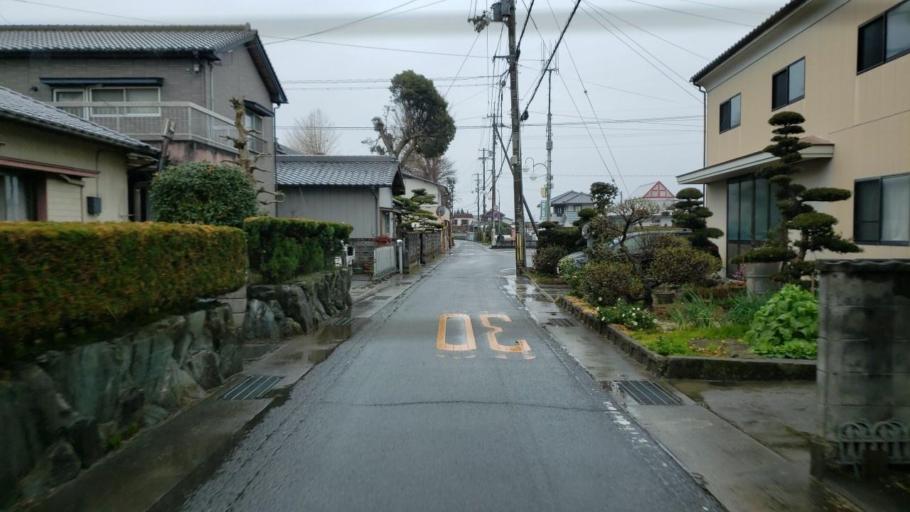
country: JP
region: Tokushima
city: Kamojimacho-jogejima
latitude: 34.0593
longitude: 134.2905
